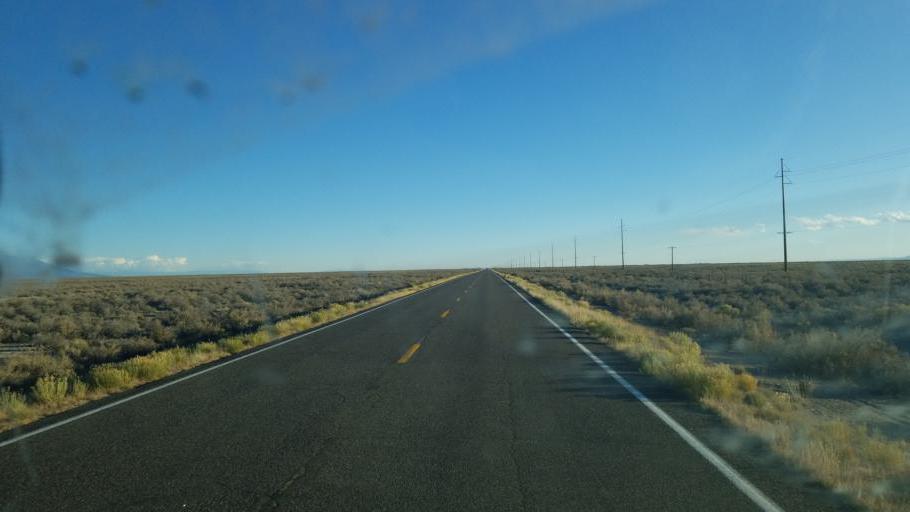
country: US
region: Colorado
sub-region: Saguache County
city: Center
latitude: 37.9402
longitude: -105.9020
